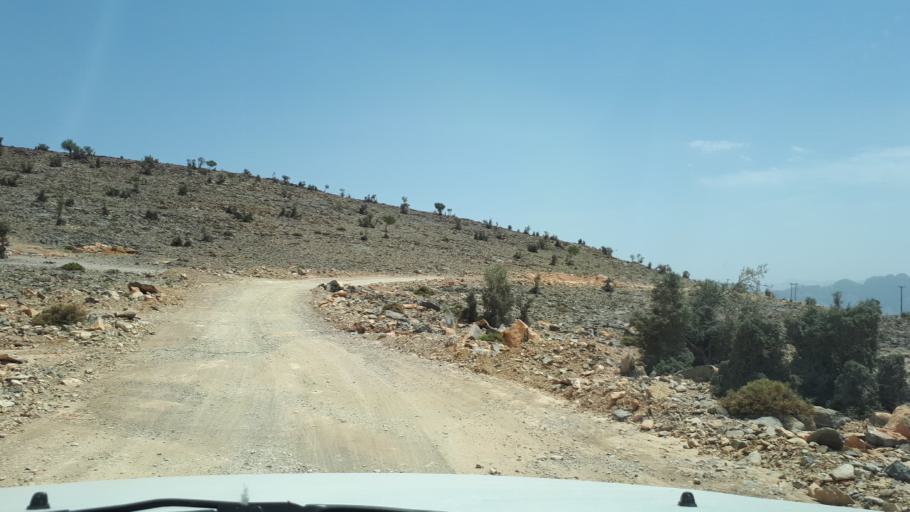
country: OM
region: Muhafazat ad Dakhiliyah
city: Bahla'
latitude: 23.2001
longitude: 57.2013
